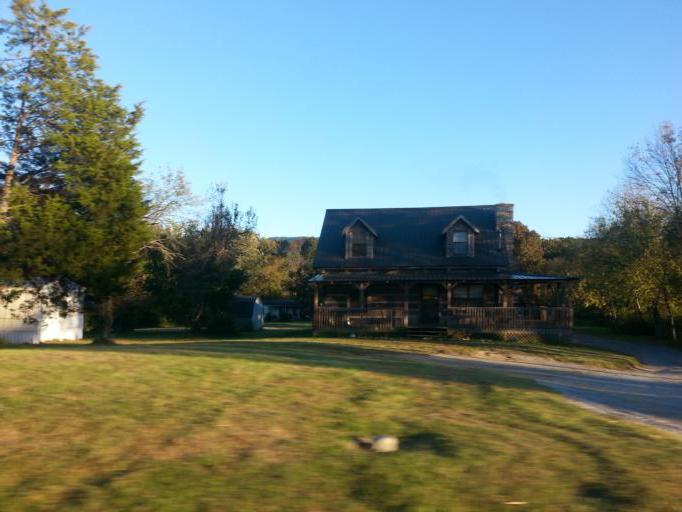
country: US
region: Tennessee
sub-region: Blount County
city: Wildwood
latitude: 35.7934
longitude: -83.8180
